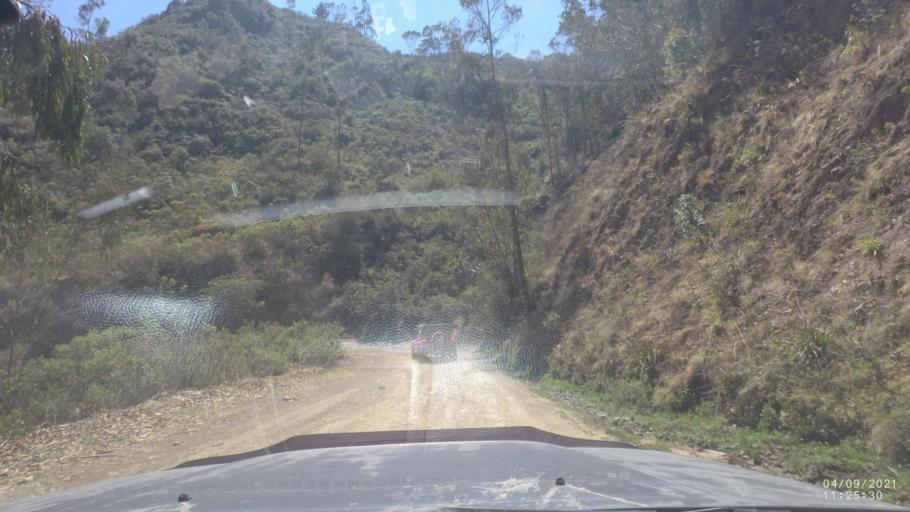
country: BO
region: Cochabamba
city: Colchani
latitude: -17.2557
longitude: -66.5114
